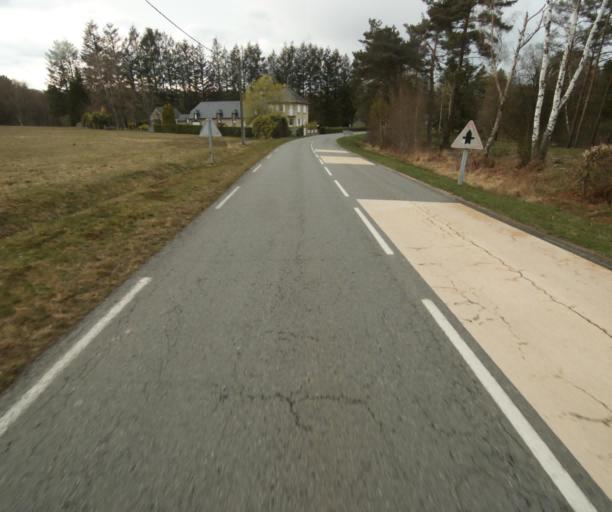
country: FR
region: Limousin
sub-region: Departement de la Correze
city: Saint-Privat
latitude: 45.2115
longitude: 2.0033
